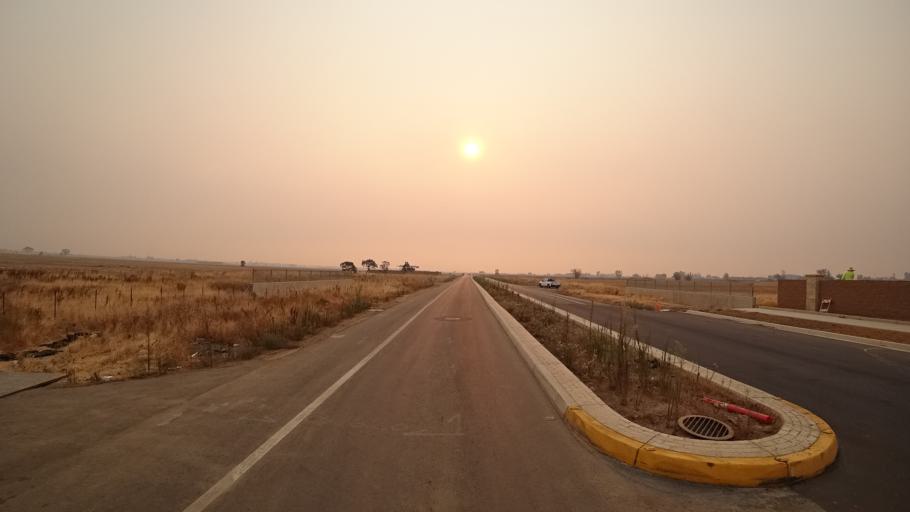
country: US
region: California
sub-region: Sacramento County
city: Laguna
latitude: 38.3796
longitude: -121.4117
